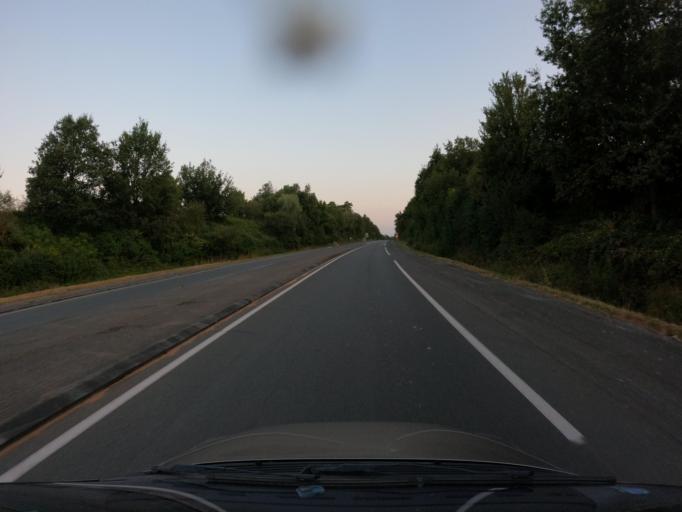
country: FR
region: Pays de la Loire
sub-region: Departement de Maine-et-Loire
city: Segre
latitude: 47.6838
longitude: -0.8567
